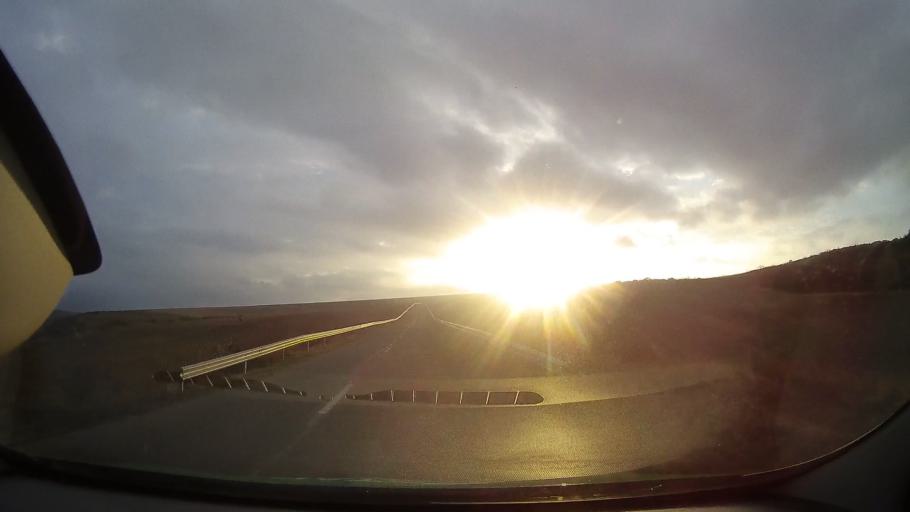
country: RO
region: Constanta
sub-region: Comuna Adamclisi
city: Adamclisi
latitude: 44.0380
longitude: 27.9407
